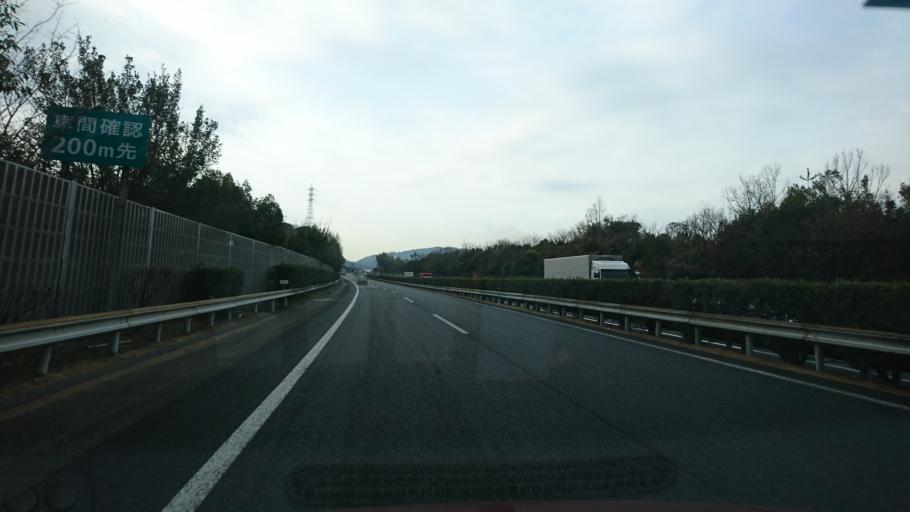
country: JP
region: Okayama
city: Kamogatacho-kamogata
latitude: 34.5470
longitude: 133.5702
